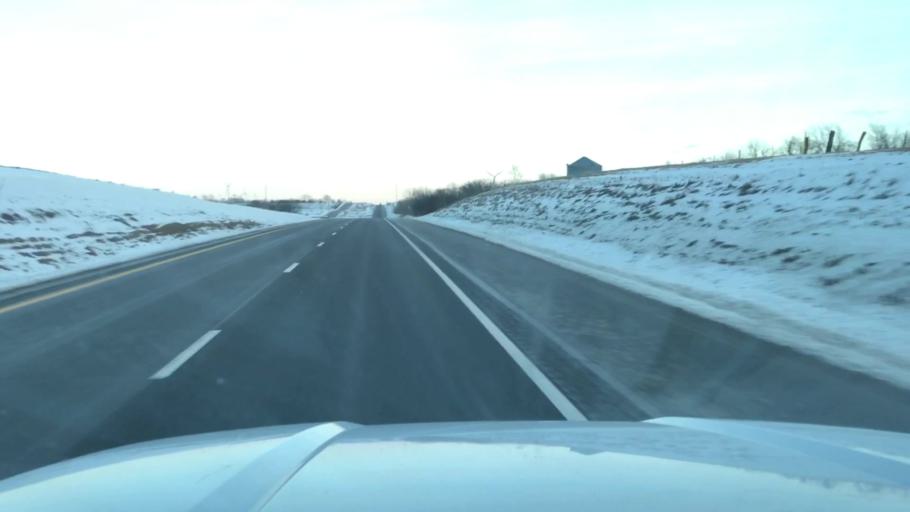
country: US
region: Missouri
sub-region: DeKalb County
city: Maysville
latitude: 39.7619
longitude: -94.4638
